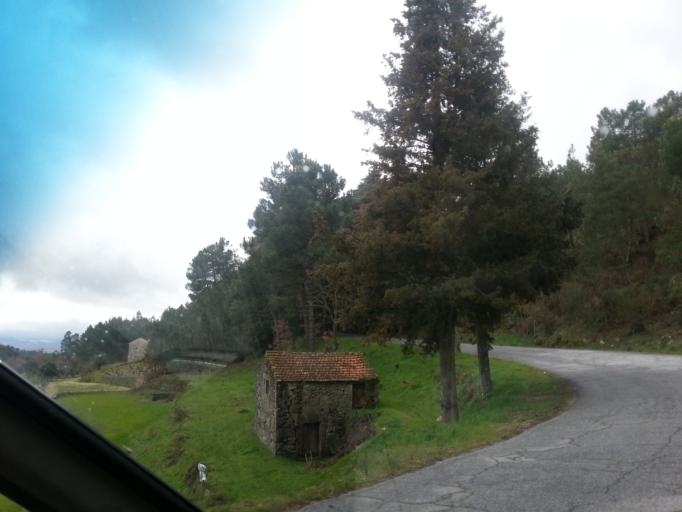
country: PT
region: Guarda
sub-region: Fornos de Algodres
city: Fornos de Algodres
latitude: 40.6120
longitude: -7.5764
